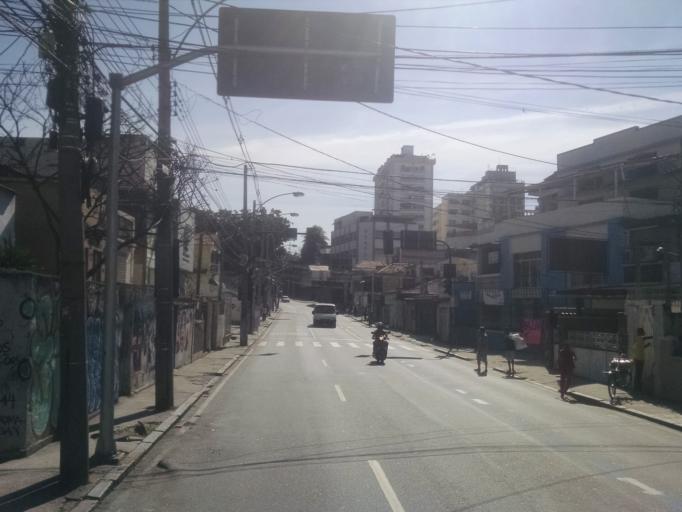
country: BR
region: Rio de Janeiro
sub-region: Rio De Janeiro
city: Rio de Janeiro
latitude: -22.9056
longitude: -43.2770
